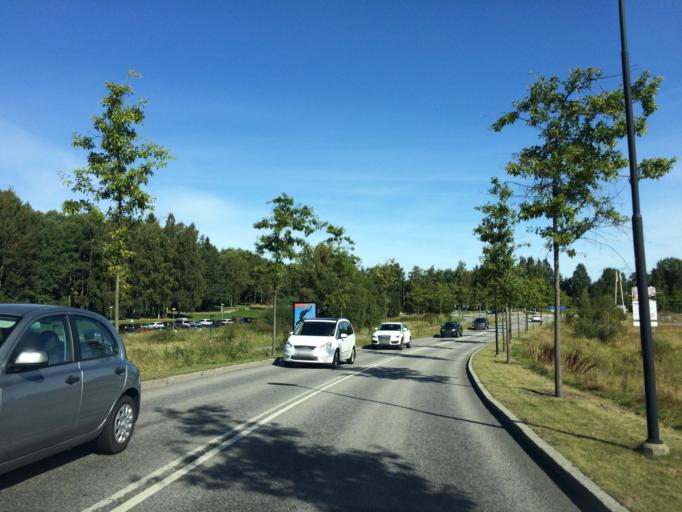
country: SE
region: Stockholm
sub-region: Stockholms Kommun
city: Kista
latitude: 59.4040
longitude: 17.9752
